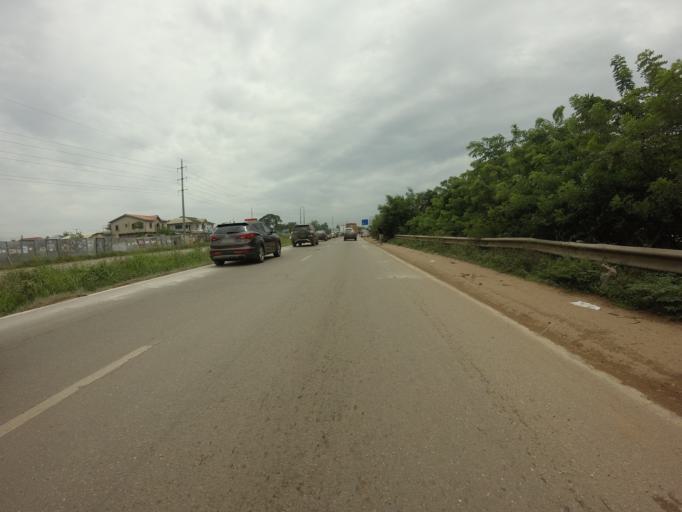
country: GH
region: Greater Accra
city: Achiaman
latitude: 5.7016
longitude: -0.2952
